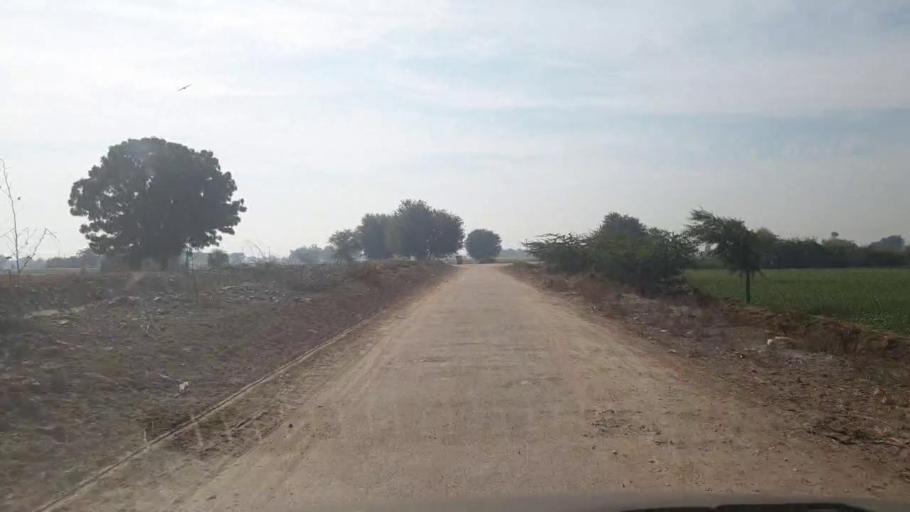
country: PK
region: Sindh
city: Shahpur Chakar
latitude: 26.1858
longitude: 68.5834
